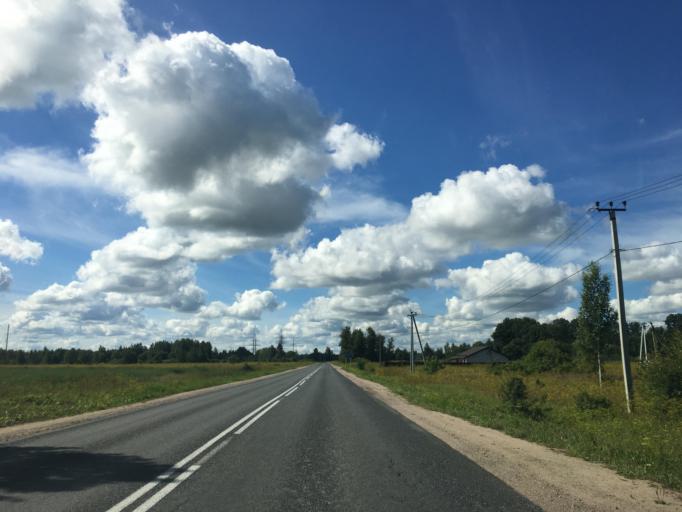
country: RU
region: Pskov
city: Pskov
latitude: 57.7788
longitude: 28.1678
